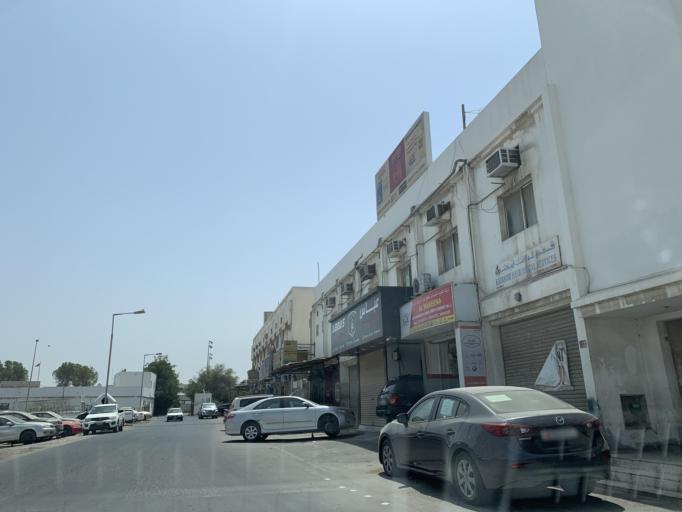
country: BH
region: Northern
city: Madinat `Isa
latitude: 26.1903
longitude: 50.5553
